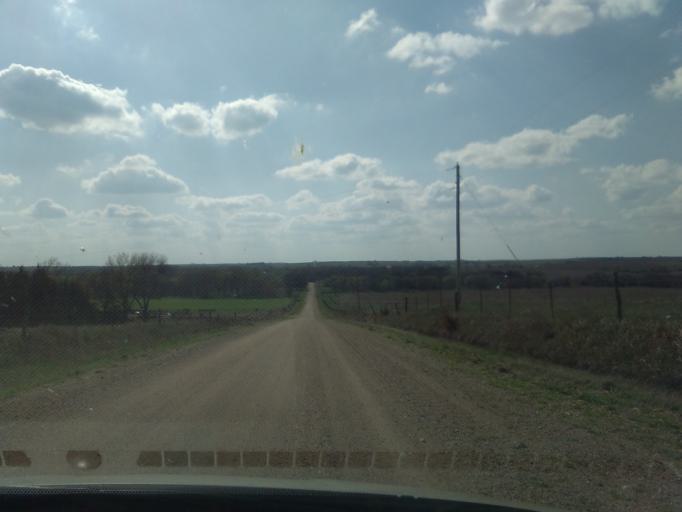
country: US
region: Nebraska
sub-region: Webster County
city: Red Cloud
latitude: 40.0313
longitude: -98.4503
